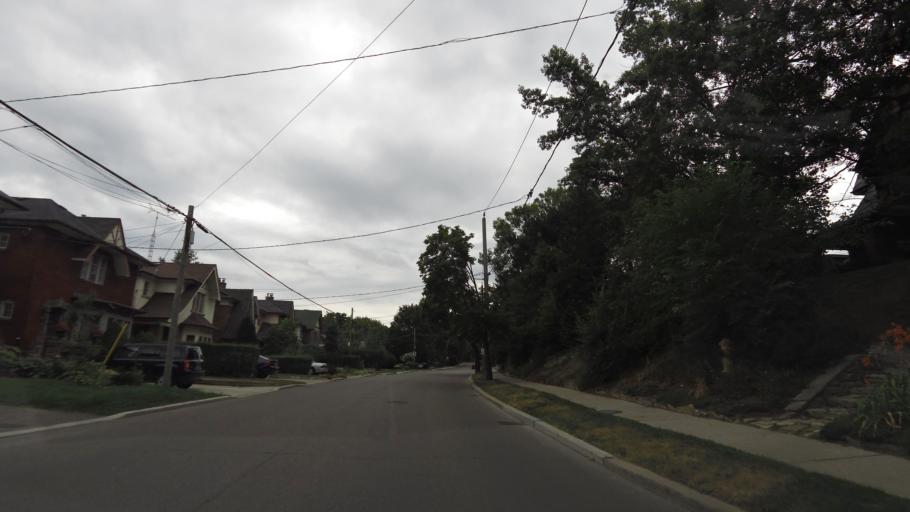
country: CA
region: Ontario
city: Toronto
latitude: 43.6426
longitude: -79.4711
